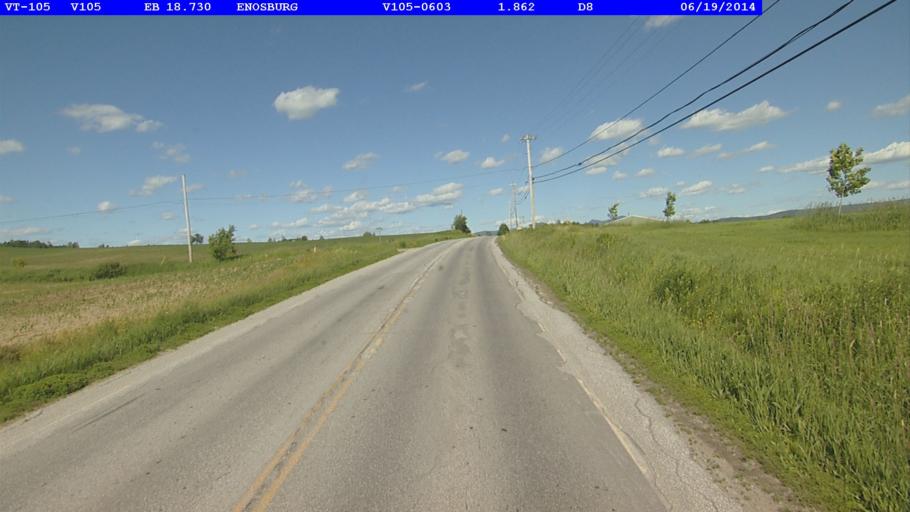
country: US
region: Vermont
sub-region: Franklin County
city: Enosburg Falls
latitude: 44.9151
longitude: -72.7903
